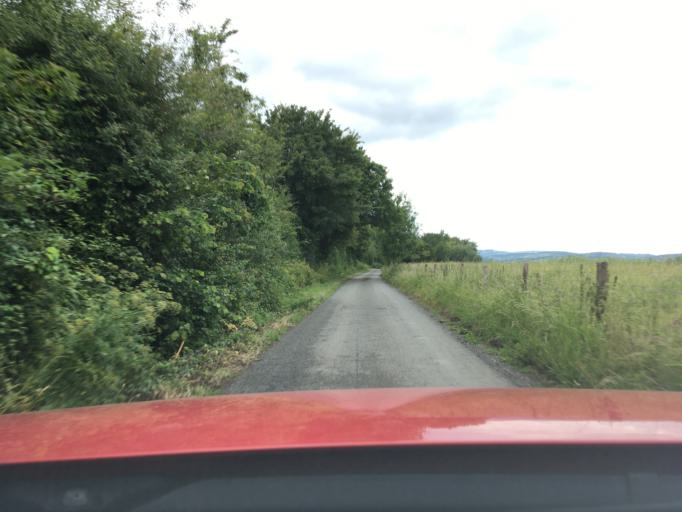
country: GB
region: England
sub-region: Gloucestershire
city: Stonehouse
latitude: 51.7937
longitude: -2.3787
